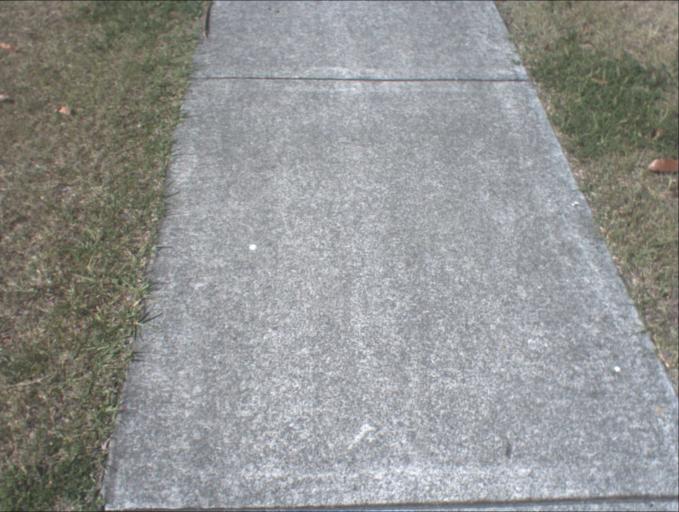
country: AU
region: Queensland
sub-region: Logan
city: Slacks Creek
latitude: -27.6541
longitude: 153.1822
